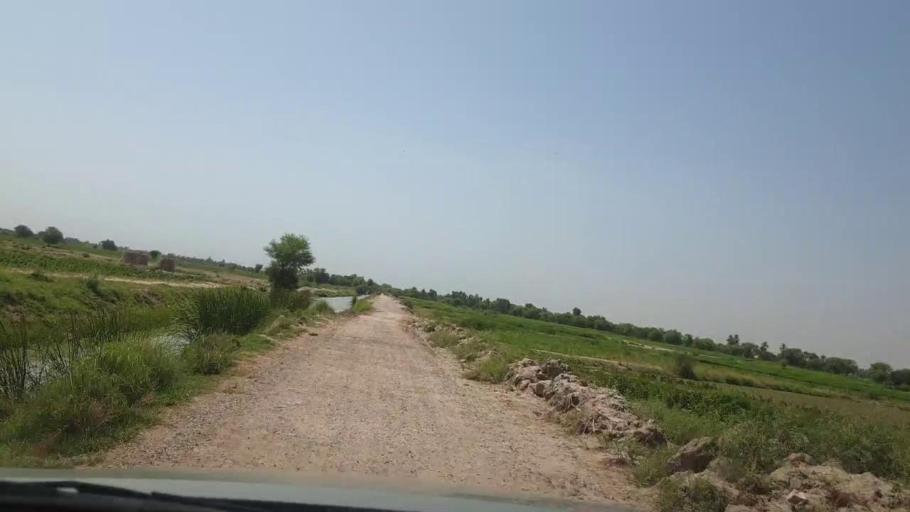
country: PK
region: Sindh
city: Rohri
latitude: 27.6616
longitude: 68.9812
